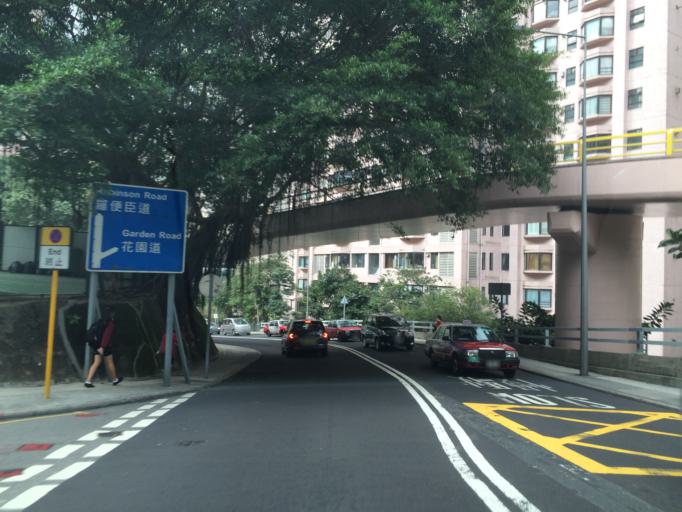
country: HK
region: Central and Western
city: Central
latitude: 22.2748
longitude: 114.1564
